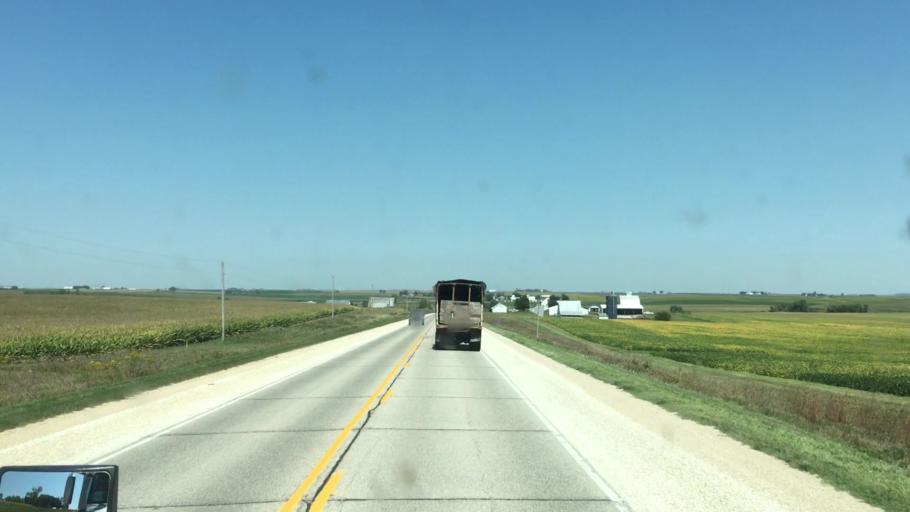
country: US
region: Iowa
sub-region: Tama County
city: Dysart
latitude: 42.0577
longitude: -92.2987
